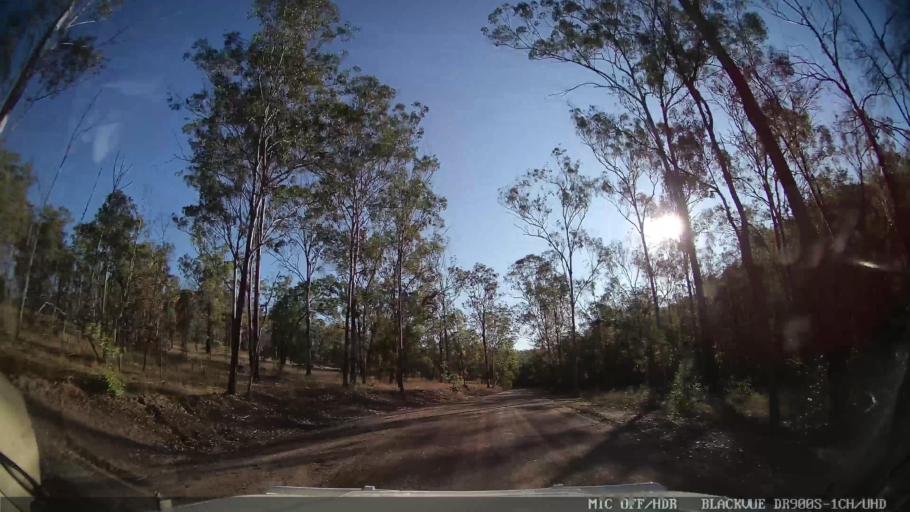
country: AU
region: Queensland
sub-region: Gladstone
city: Toolooa
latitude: -24.6954
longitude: 151.4082
